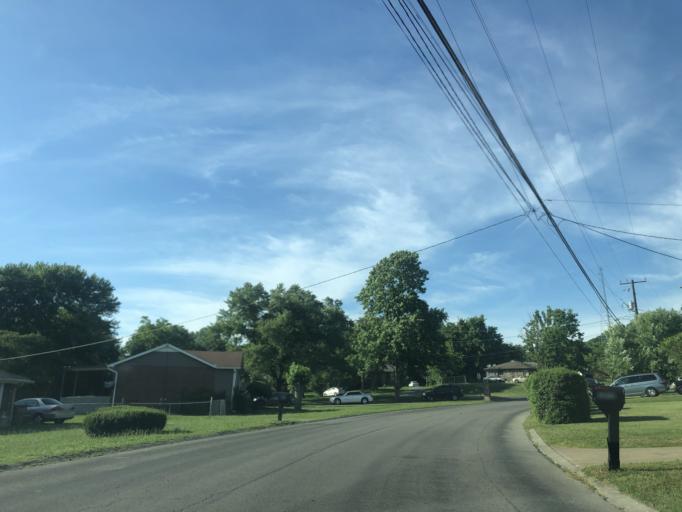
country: US
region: Tennessee
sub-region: Davidson County
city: Nashville
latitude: 36.2228
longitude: -86.8503
